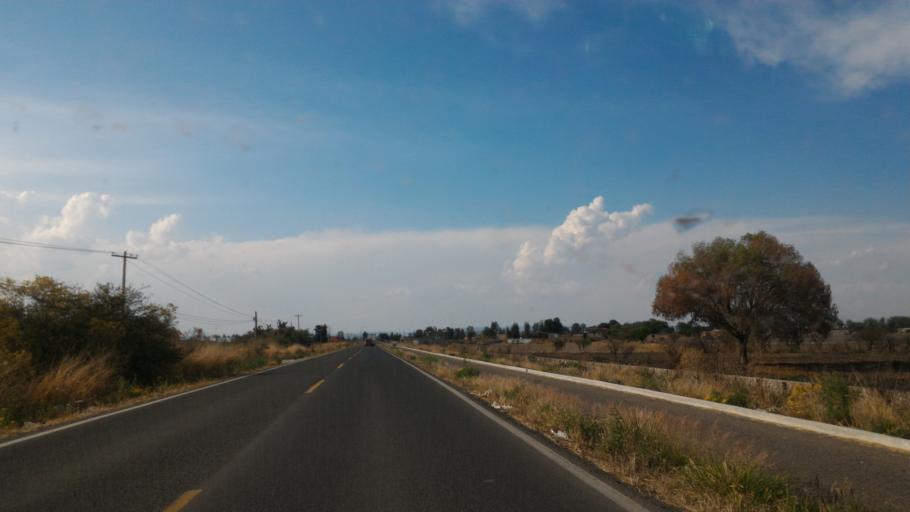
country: MX
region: Guanajuato
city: Ciudad Manuel Doblado
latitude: 20.7507
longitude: -101.9621
